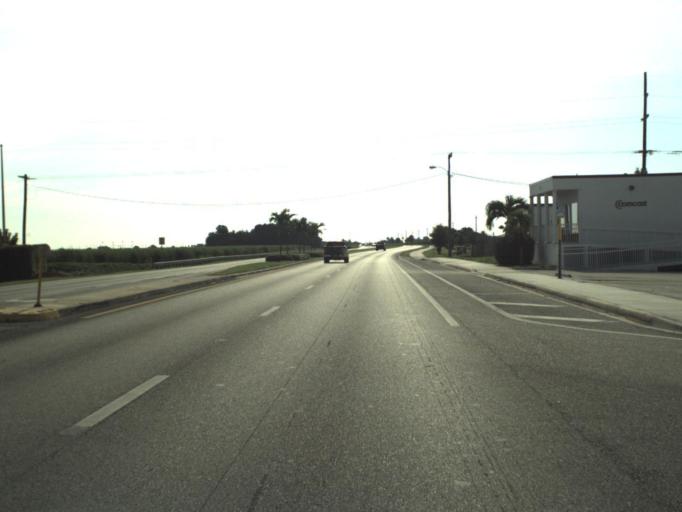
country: US
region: Florida
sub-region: Palm Beach County
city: South Bay
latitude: 26.6642
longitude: -80.7091
